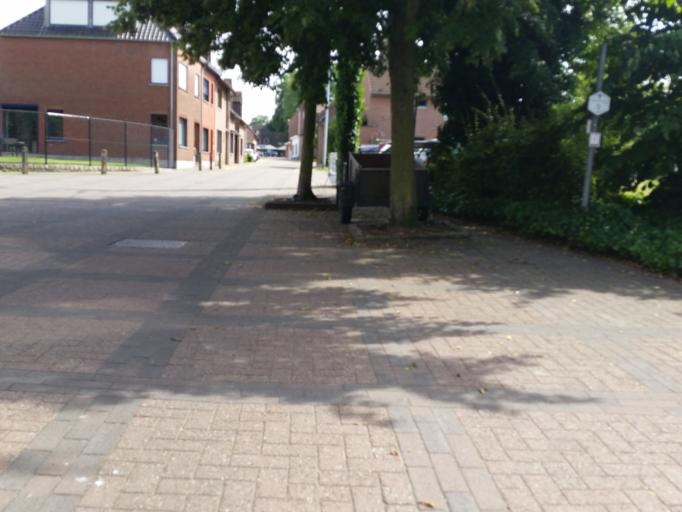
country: BE
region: Flanders
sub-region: Provincie Antwerpen
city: Niel
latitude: 51.1081
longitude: 4.2990
